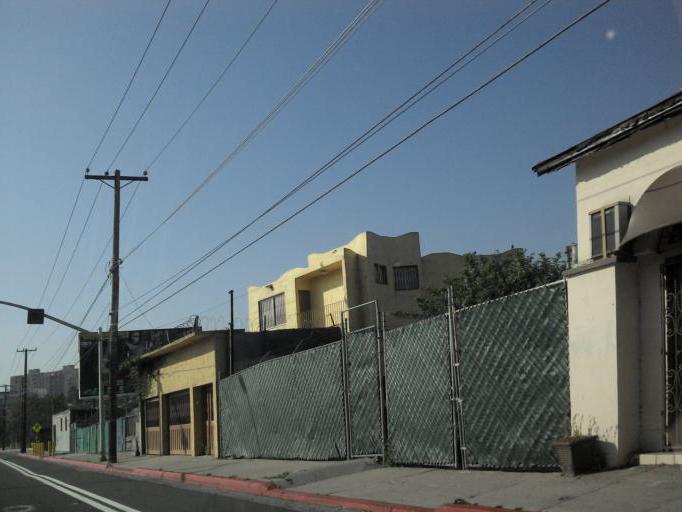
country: MX
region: Baja California
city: Tijuana
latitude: 32.5158
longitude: -117.0001
